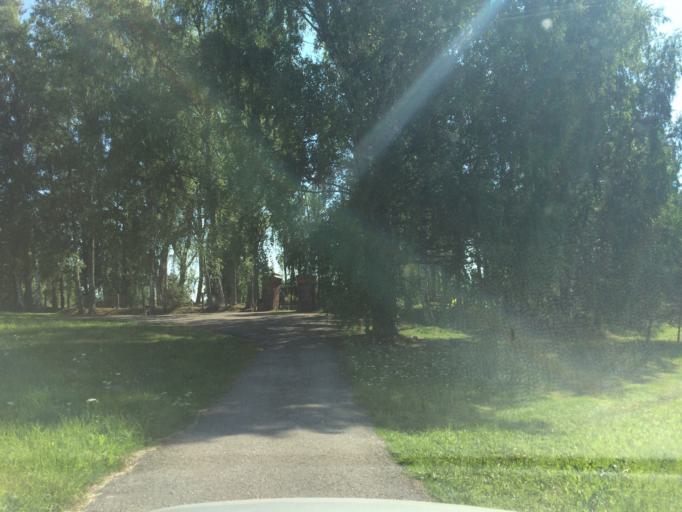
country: LV
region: Rezekne
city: Rezekne
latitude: 56.4888
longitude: 27.1407
